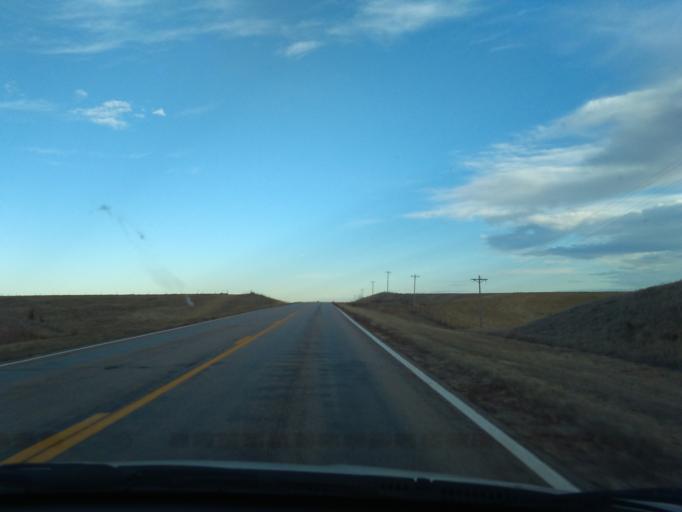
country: US
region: Nebraska
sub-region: Phelps County
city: Holdrege
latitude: 40.3072
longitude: -99.3574
